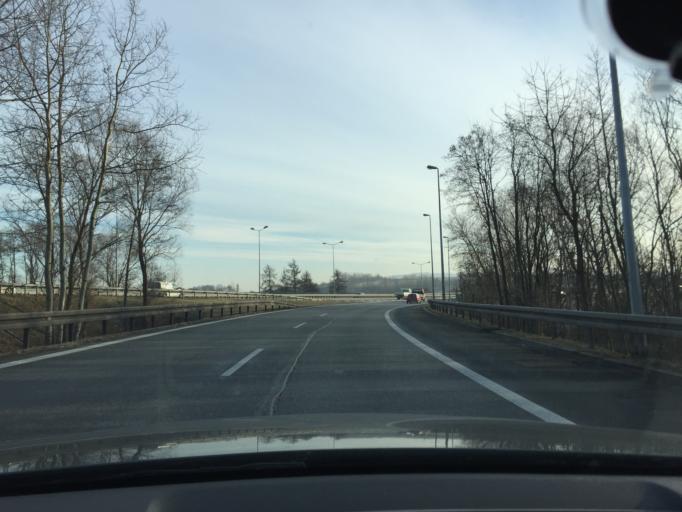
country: PL
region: Lesser Poland Voivodeship
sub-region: Powiat krakowski
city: Balice
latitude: 50.0858
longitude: 19.8064
